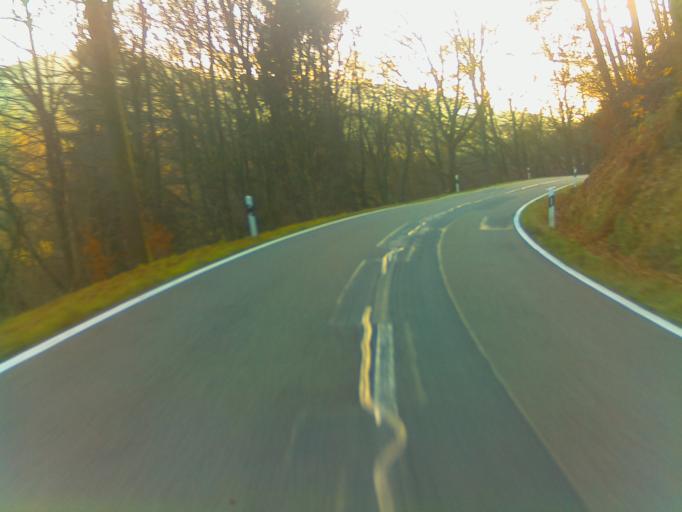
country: DE
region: Hesse
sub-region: Regierungsbezirk Darmstadt
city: Hesseneck
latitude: 49.5448
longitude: 9.0846
